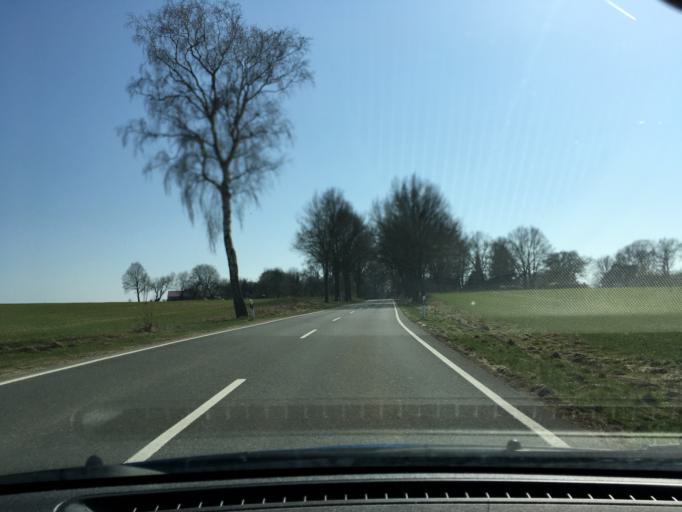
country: DE
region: Lower Saxony
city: Rehlingen
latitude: 53.1029
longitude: 10.2601
